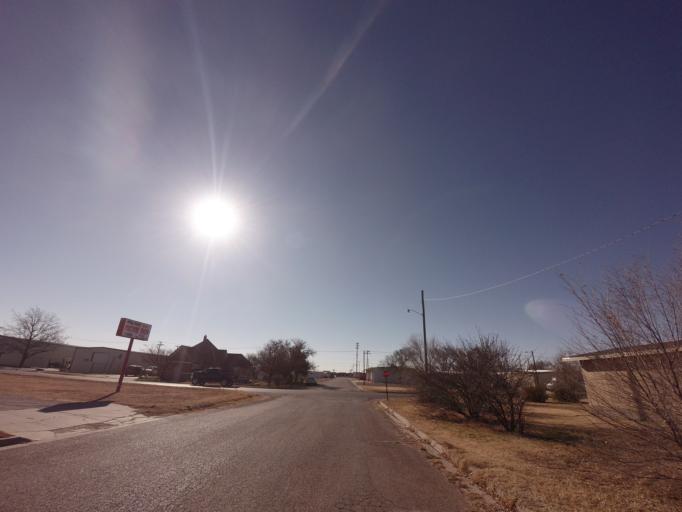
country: US
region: New Mexico
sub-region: Curry County
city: Clovis
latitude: 34.4011
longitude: -103.1902
